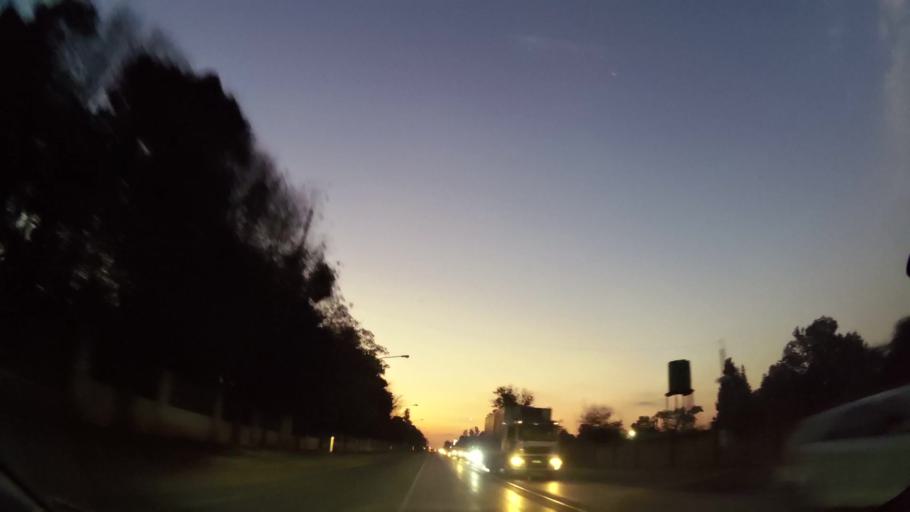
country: ZA
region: Gauteng
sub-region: Ekurhuleni Metropolitan Municipality
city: Benoni
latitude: -26.0970
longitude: 28.3111
